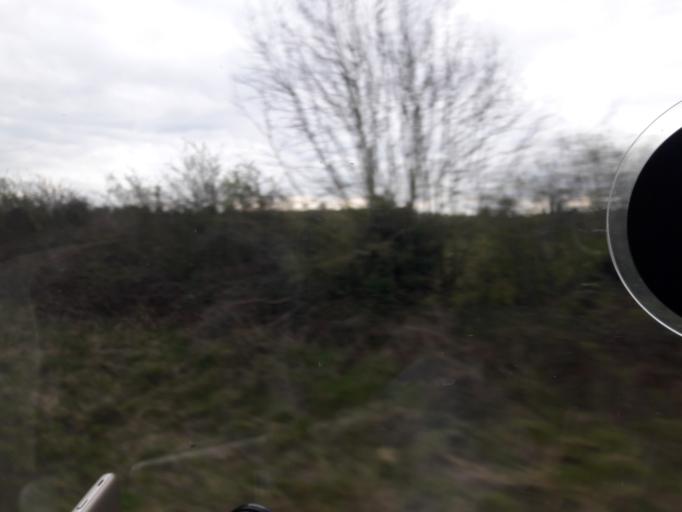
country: IE
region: Leinster
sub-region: An Longfort
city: Edgeworthstown
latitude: 53.6746
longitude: -7.5257
